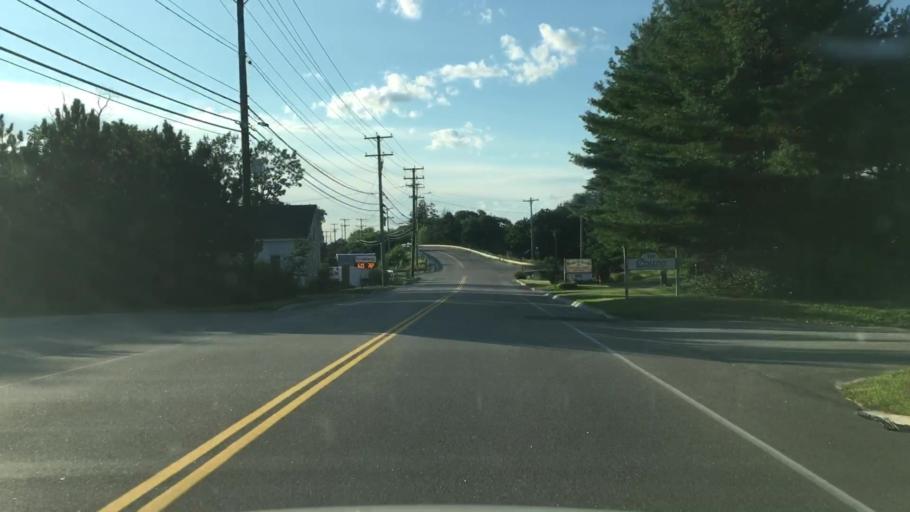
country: US
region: Maine
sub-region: Cumberland County
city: Scarborough
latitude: 43.6012
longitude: -70.2997
